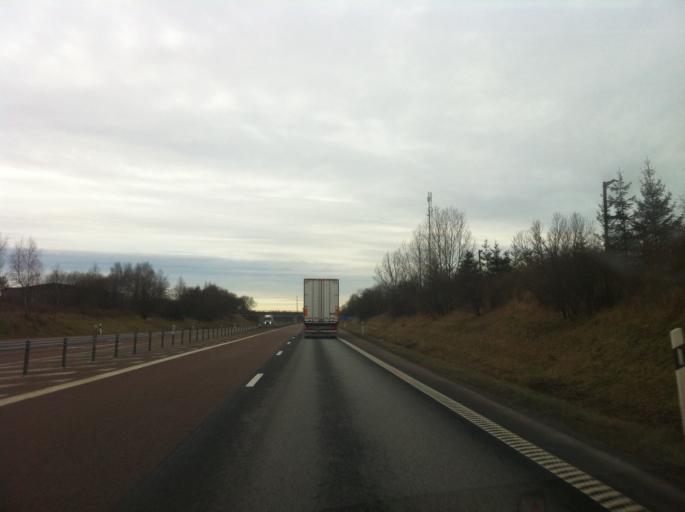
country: SE
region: Skane
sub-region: Astorps Kommun
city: Astorp
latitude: 56.1412
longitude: 12.9718
